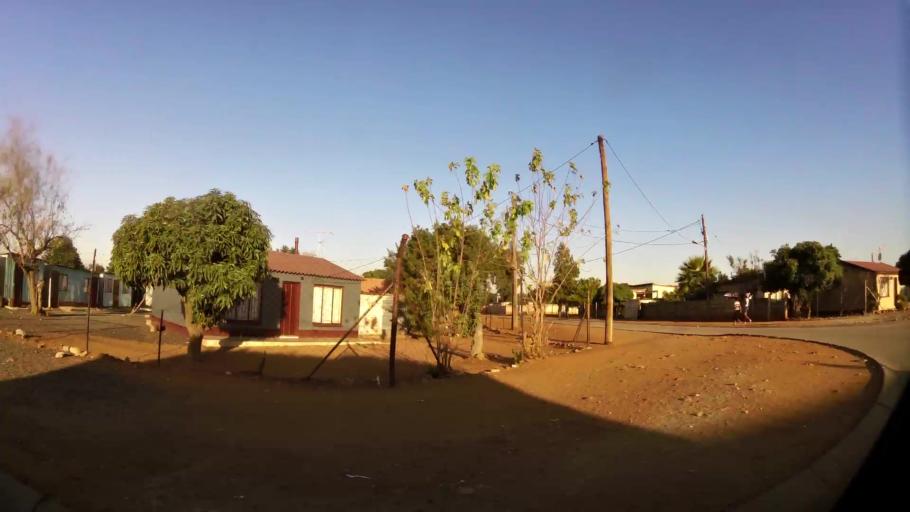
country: ZA
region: North-West
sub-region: Bojanala Platinum District Municipality
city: Rustenburg
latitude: -25.6317
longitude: 27.2105
